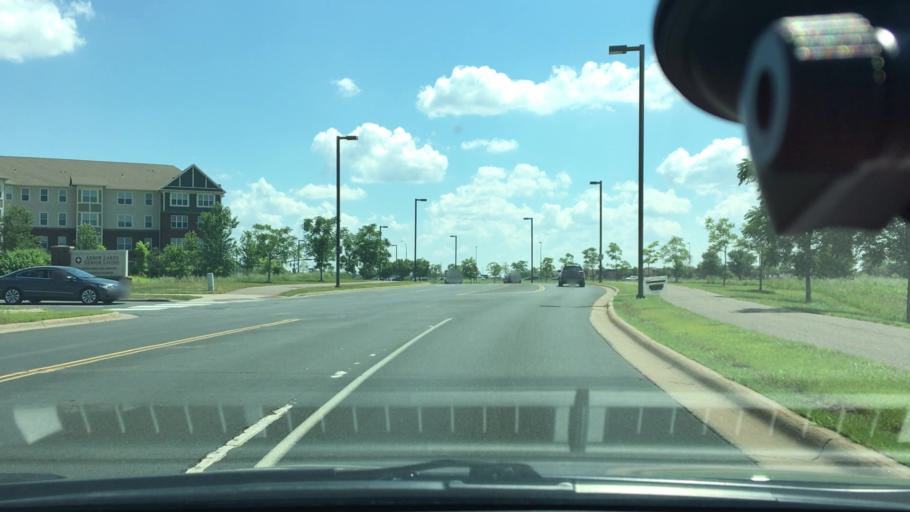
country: US
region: Minnesota
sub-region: Hennepin County
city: Maple Grove
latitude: 45.0982
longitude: -93.4346
